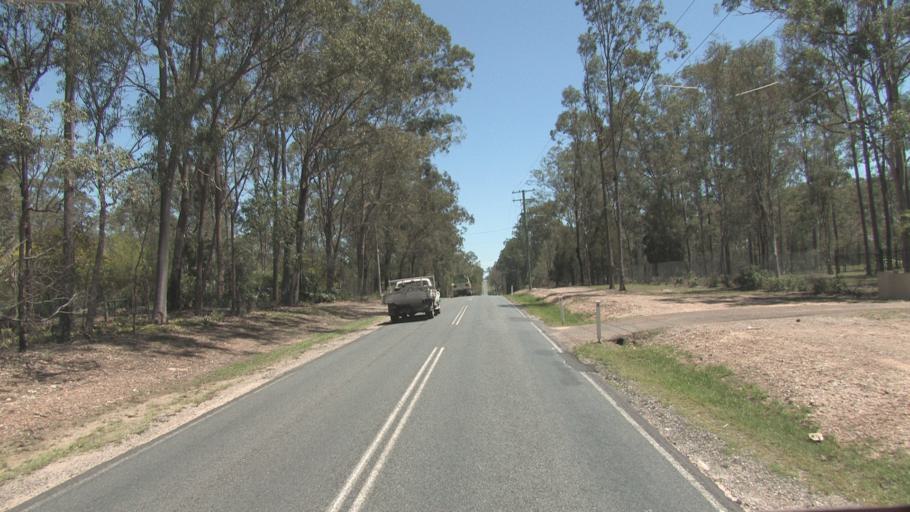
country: AU
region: Queensland
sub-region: Logan
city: Park Ridge South
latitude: -27.7001
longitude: 153.0519
